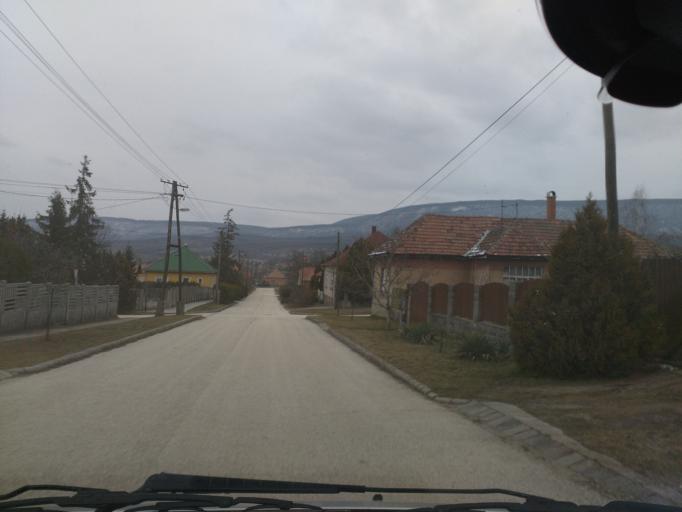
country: HU
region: Komarom-Esztergom
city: Piliscsev
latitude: 47.6712
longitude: 18.8159
